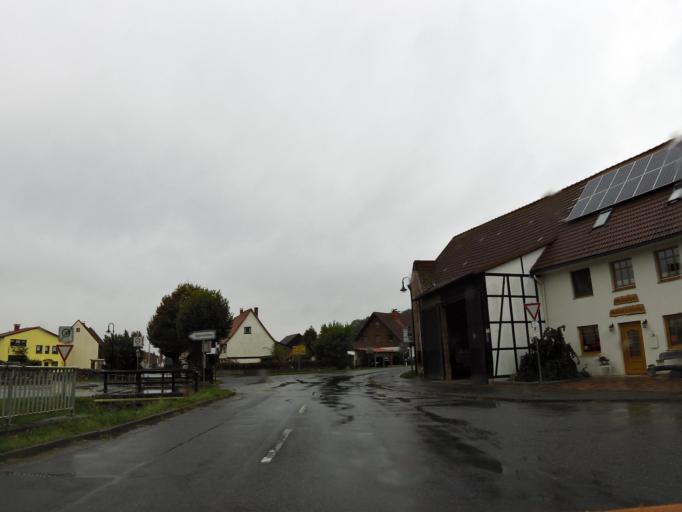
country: DE
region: Lower Saxony
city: Herzberg am Harz
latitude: 51.6303
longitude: 10.3732
